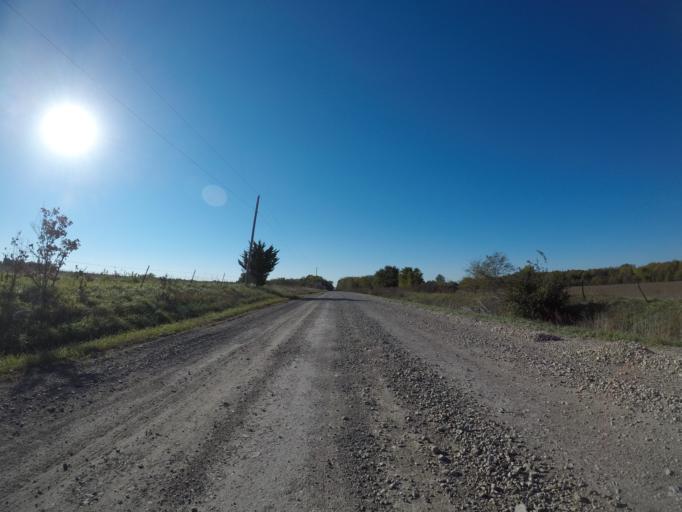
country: US
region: Kansas
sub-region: Morris County
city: Council Grove
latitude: 38.8536
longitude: -96.4829
